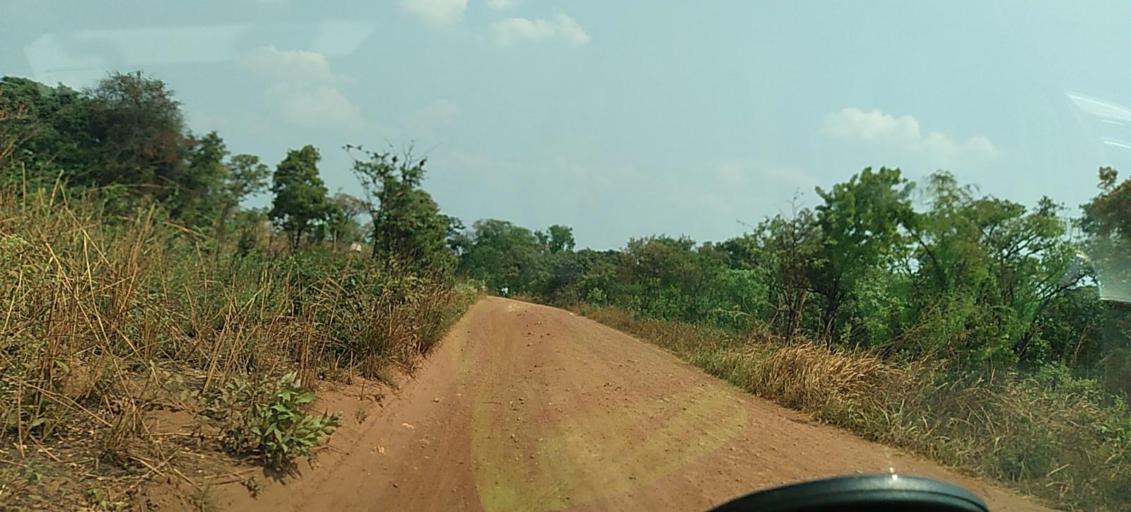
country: ZM
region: North-Western
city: Kansanshi
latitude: -12.1070
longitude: 26.3659
